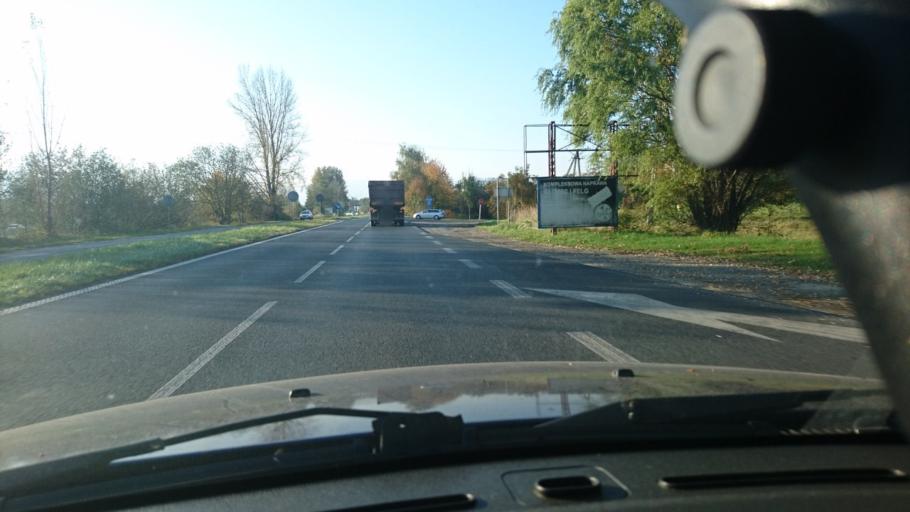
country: PL
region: Silesian Voivodeship
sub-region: Powiat cieszynski
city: Gorki Wielkie
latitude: 49.7748
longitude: 18.8086
